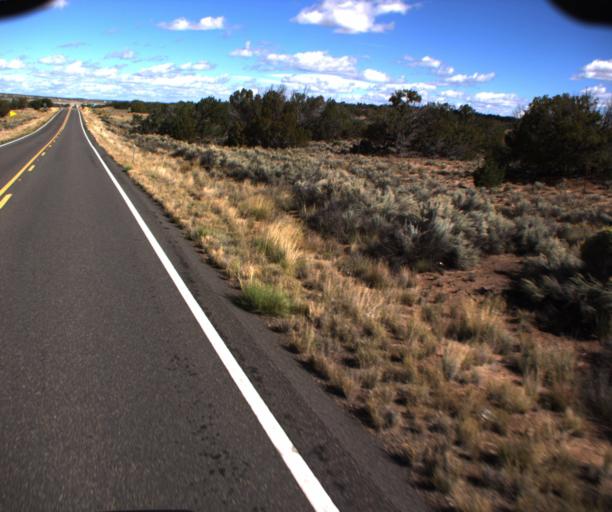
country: US
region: Arizona
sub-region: Apache County
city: Houck
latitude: 34.8975
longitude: -109.2380
